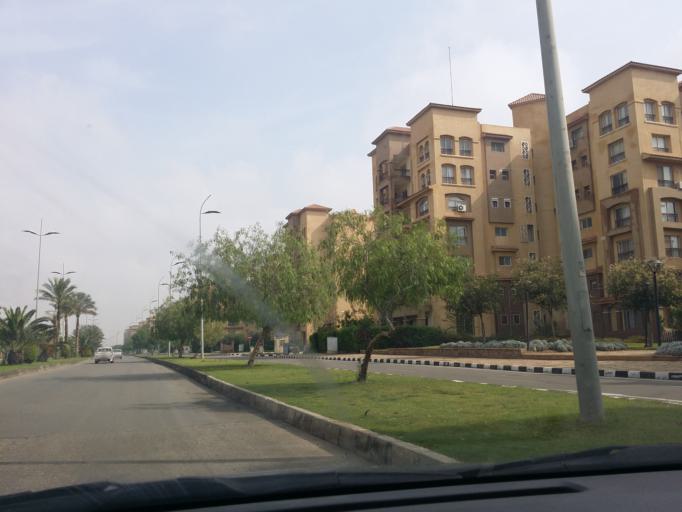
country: EG
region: Muhafazat al Qalyubiyah
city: Al Khankah
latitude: 30.0983
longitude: 31.6343
